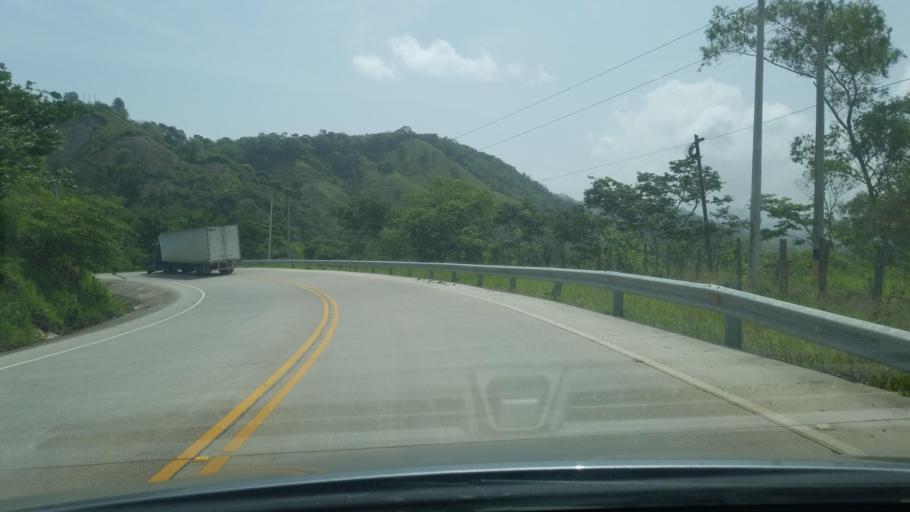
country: HN
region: Copan
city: San Jeronimo
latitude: 14.9590
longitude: -88.8962
